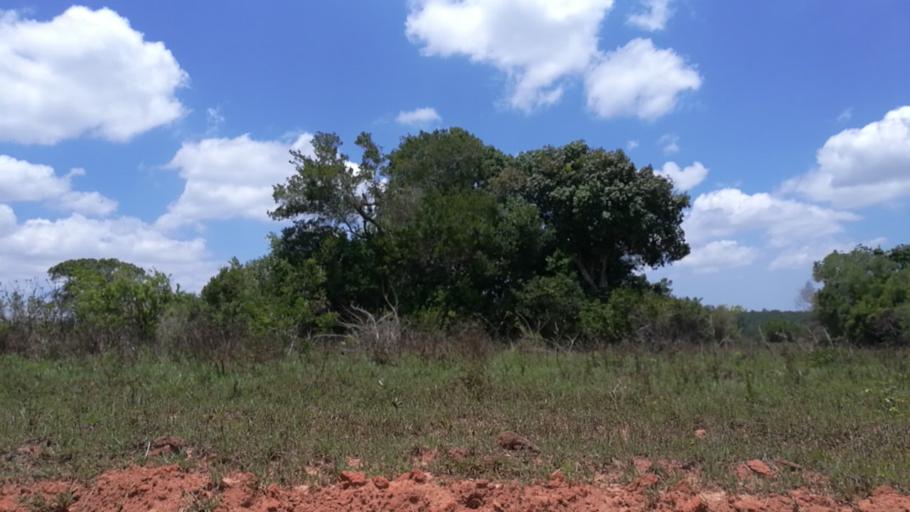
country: KE
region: Kwale
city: Kwale
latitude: -4.2337
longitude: 39.4279
